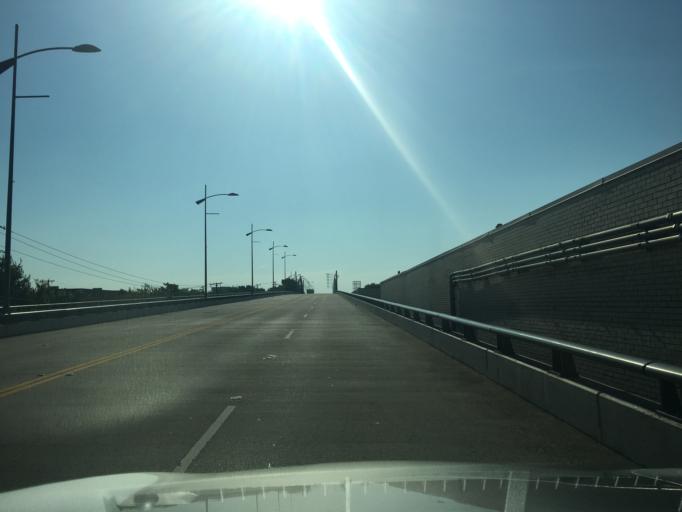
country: US
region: Texas
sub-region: Dallas County
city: Addison
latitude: 32.9564
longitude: -96.8415
